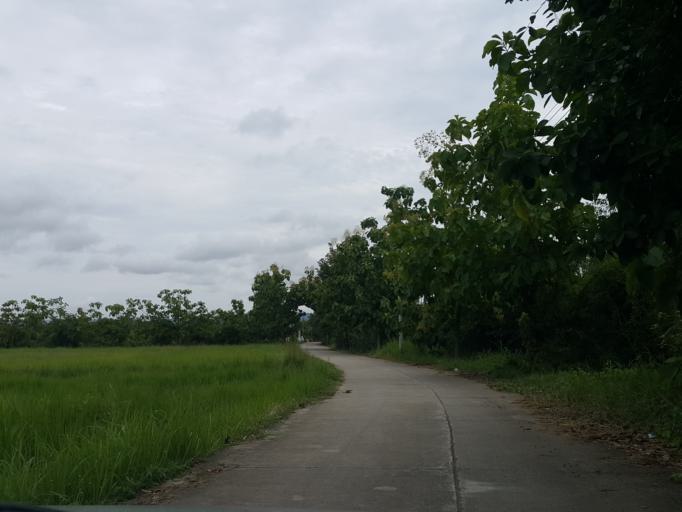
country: TH
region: Chiang Mai
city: San Sai
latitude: 18.8382
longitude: 99.1209
